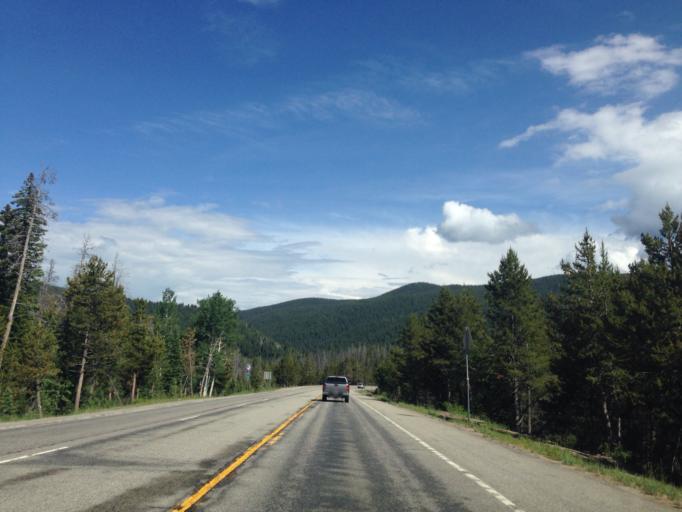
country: US
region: Colorado
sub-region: Routt County
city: Steamboat Springs
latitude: 40.3530
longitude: -106.7462
